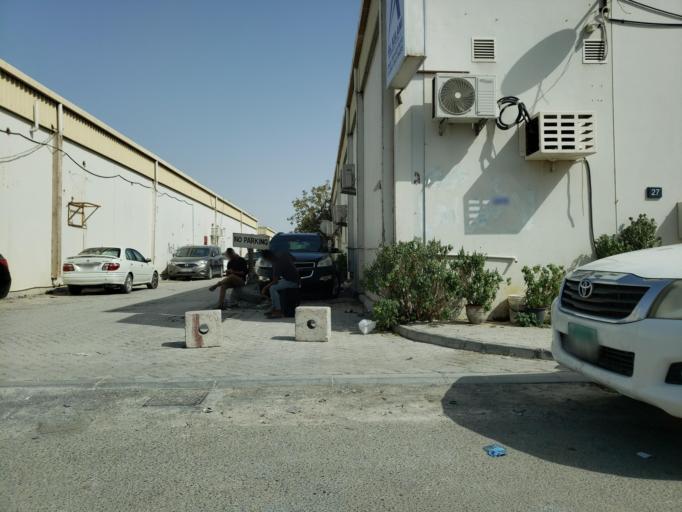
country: AE
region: Ash Shariqah
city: Sharjah
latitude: 25.3301
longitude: 55.4027
